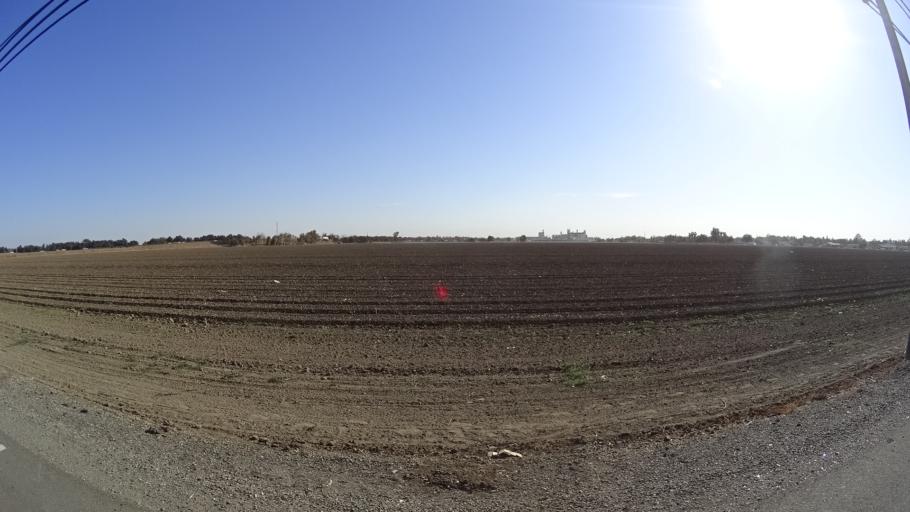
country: US
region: California
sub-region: Yolo County
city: Woodland
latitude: 38.6965
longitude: -121.7839
